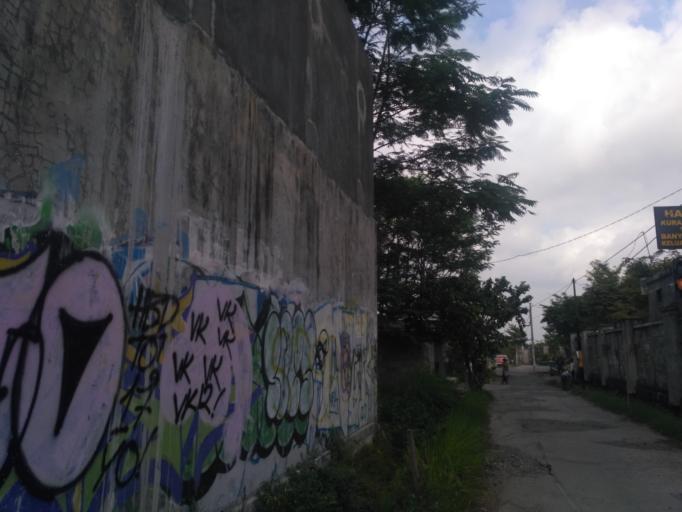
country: ID
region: Daerah Istimewa Yogyakarta
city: Melati
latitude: -7.7478
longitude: 110.3561
